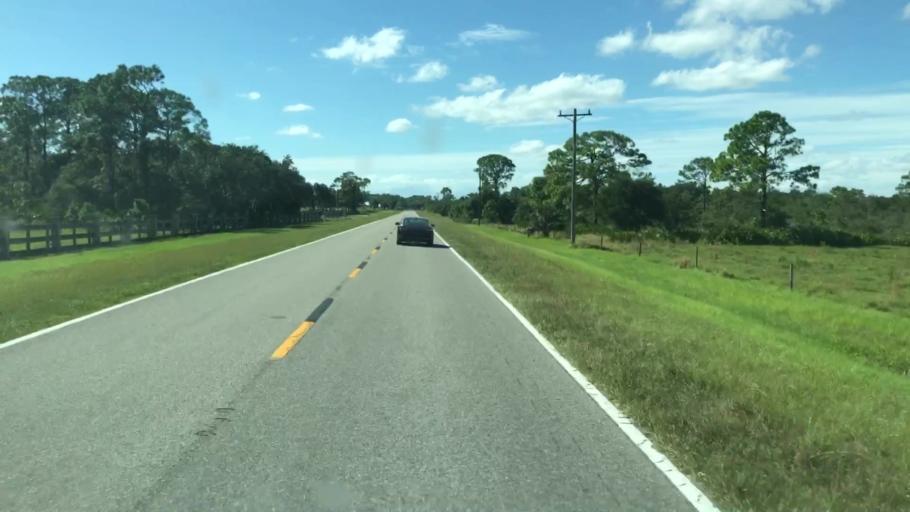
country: US
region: Florida
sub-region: Lee County
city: Fort Myers Shores
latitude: 26.7402
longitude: -81.7538
